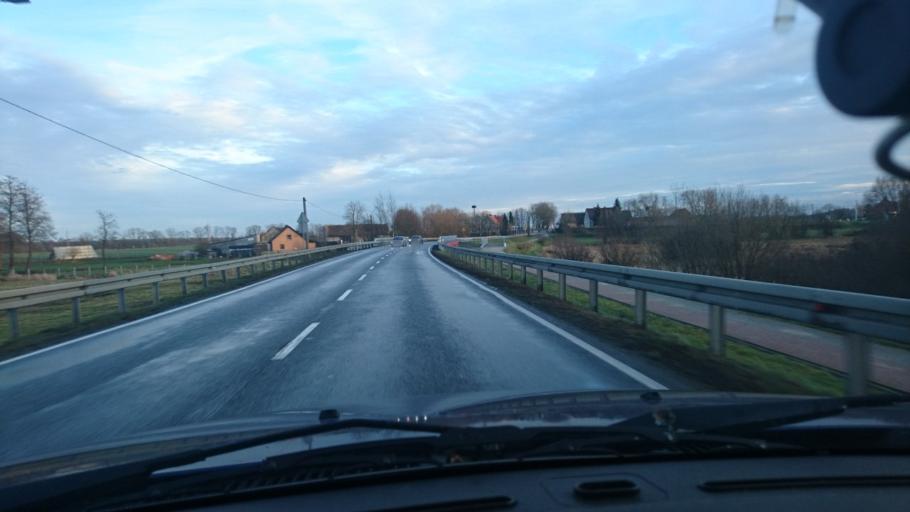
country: PL
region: Greater Poland Voivodeship
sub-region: Powiat kepinski
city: Opatow
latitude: 51.1648
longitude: 18.1503
